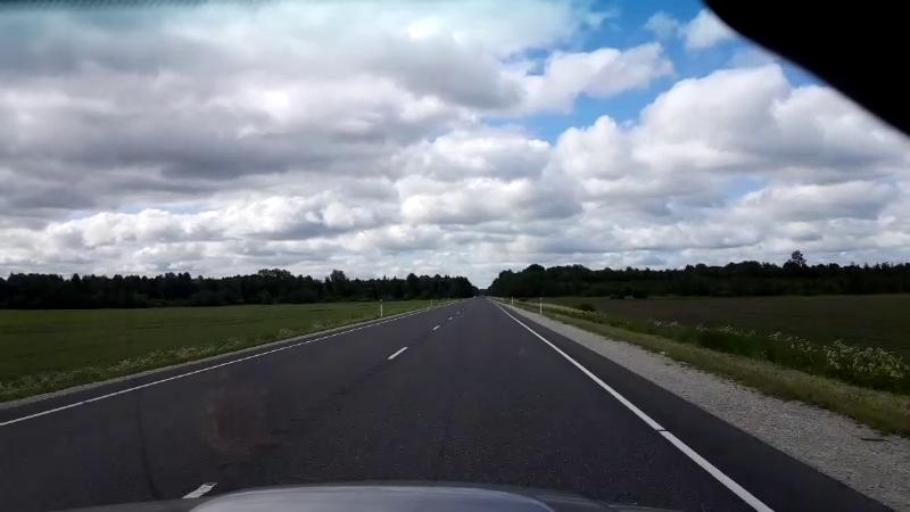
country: EE
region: Raplamaa
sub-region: Maerjamaa vald
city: Marjamaa
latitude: 58.8431
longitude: 24.4254
